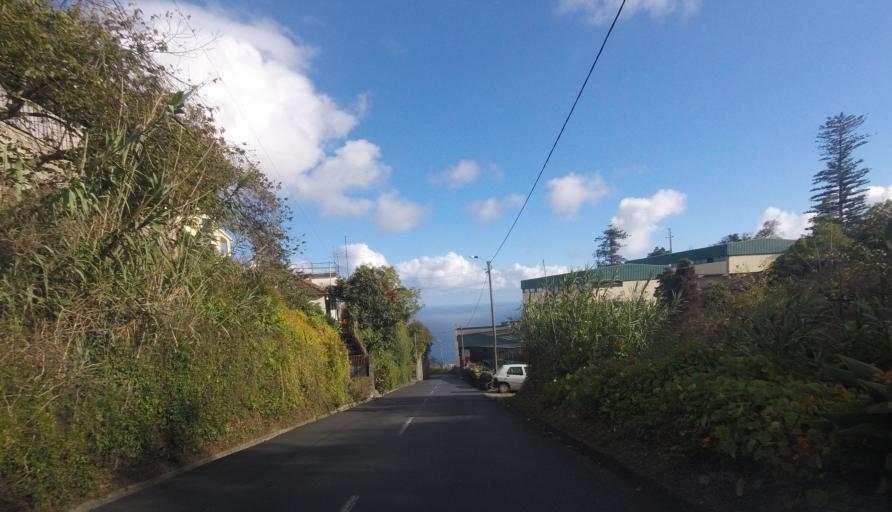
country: PT
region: Madeira
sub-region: Funchal
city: Nossa Senhora do Monte
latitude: 32.6686
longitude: -16.9027
